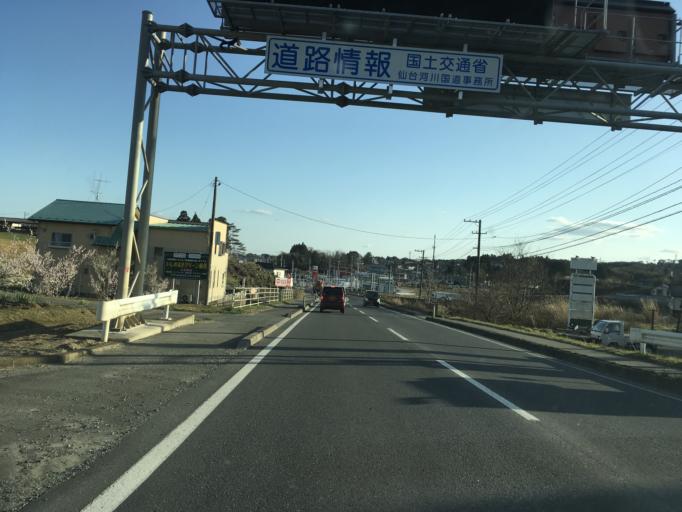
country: JP
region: Iwate
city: Ofunato
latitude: 38.8602
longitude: 141.5803
